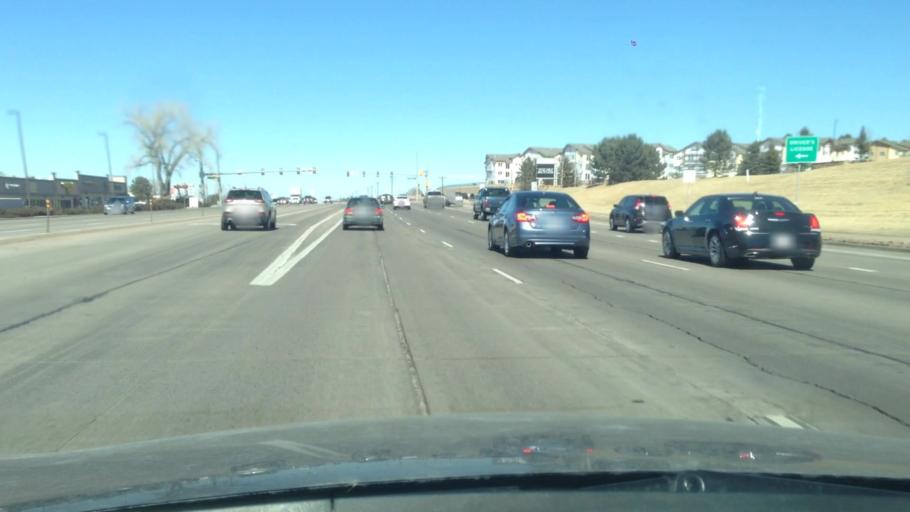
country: US
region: Colorado
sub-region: Douglas County
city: Stonegate
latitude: 39.5567
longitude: -104.7789
